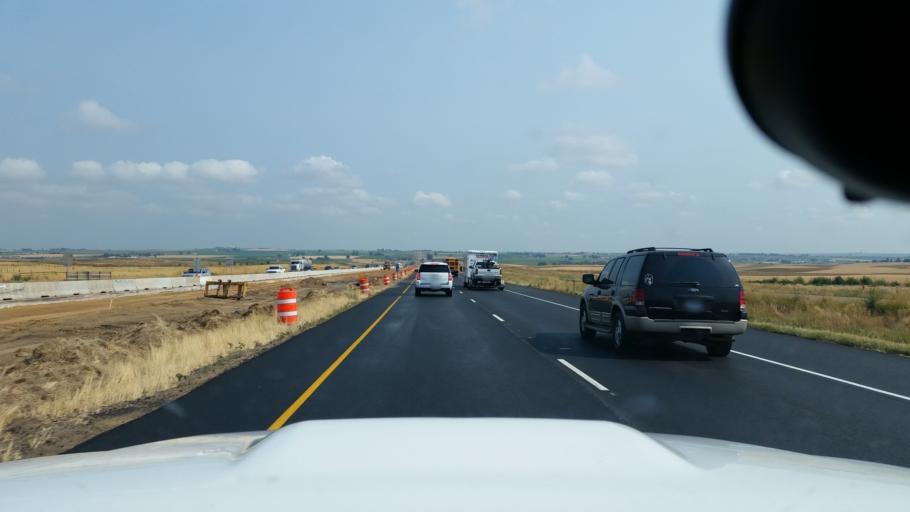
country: US
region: Colorado
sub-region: Weld County
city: Mead
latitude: 40.2761
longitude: -104.9800
